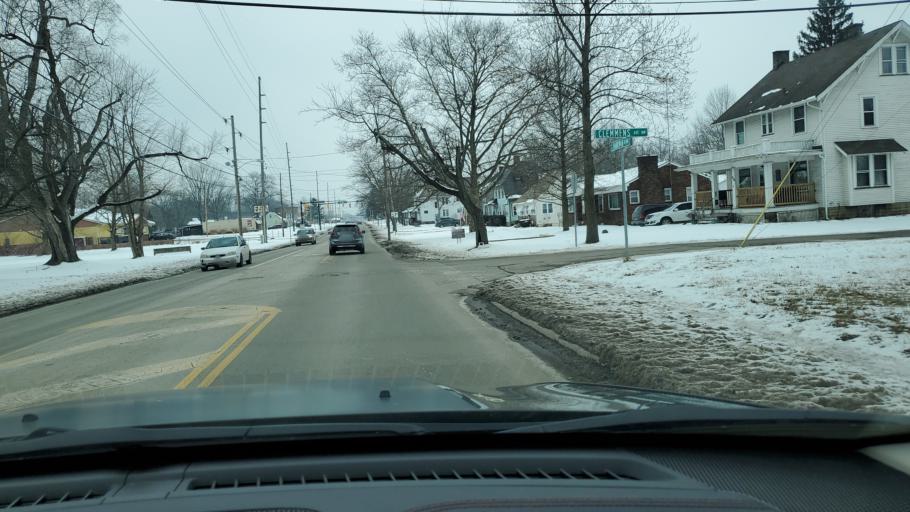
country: US
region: Ohio
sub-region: Trumbull County
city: Warren
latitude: 41.2456
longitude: -80.8444
